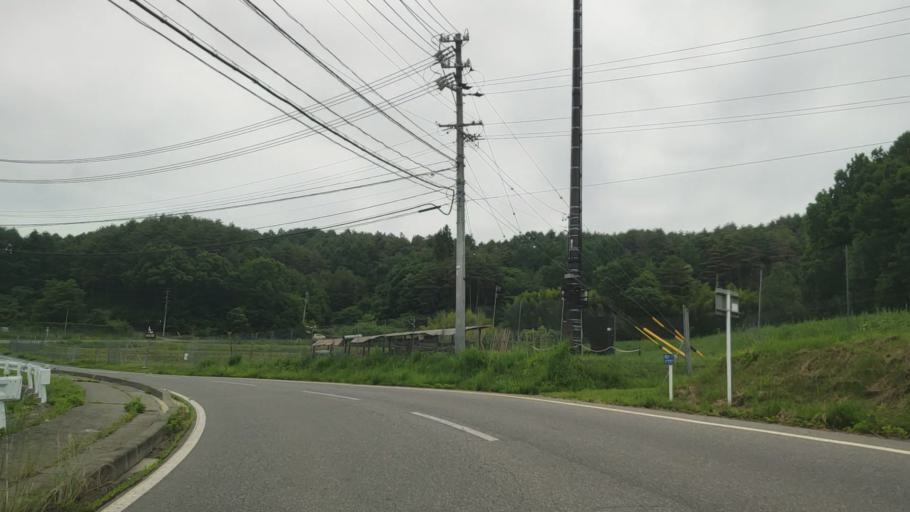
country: JP
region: Nagano
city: Kamimaruko
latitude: 36.2763
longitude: 138.2818
